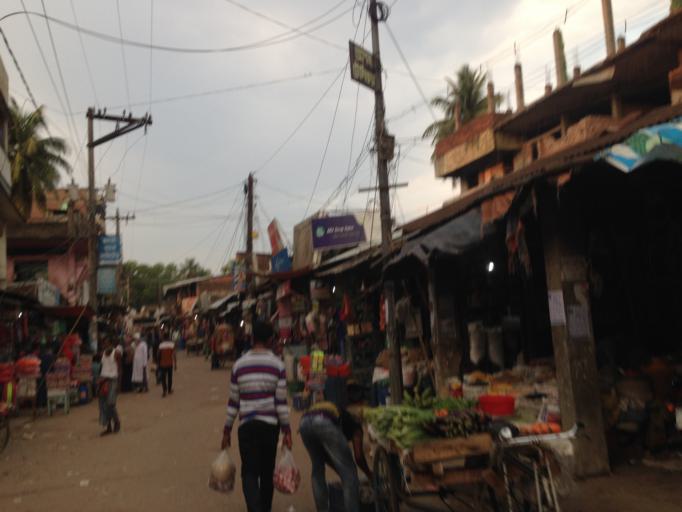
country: BD
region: Chittagong
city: Lakshmipur
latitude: 22.9688
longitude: 90.8060
